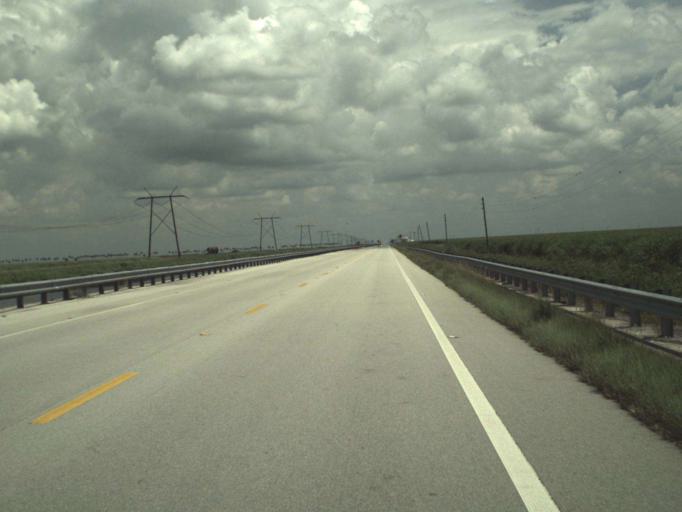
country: US
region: Florida
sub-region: Palm Beach County
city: Pahokee
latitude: 26.8226
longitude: -80.5764
